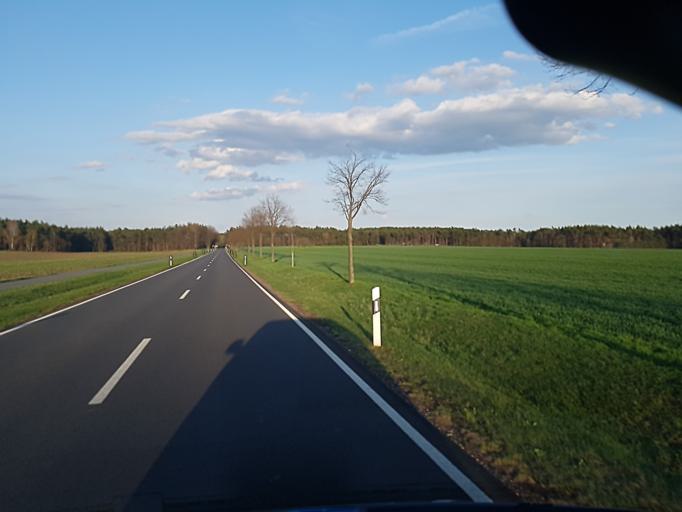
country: DE
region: Saxony
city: Kossa
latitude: 51.5770
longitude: 12.7192
